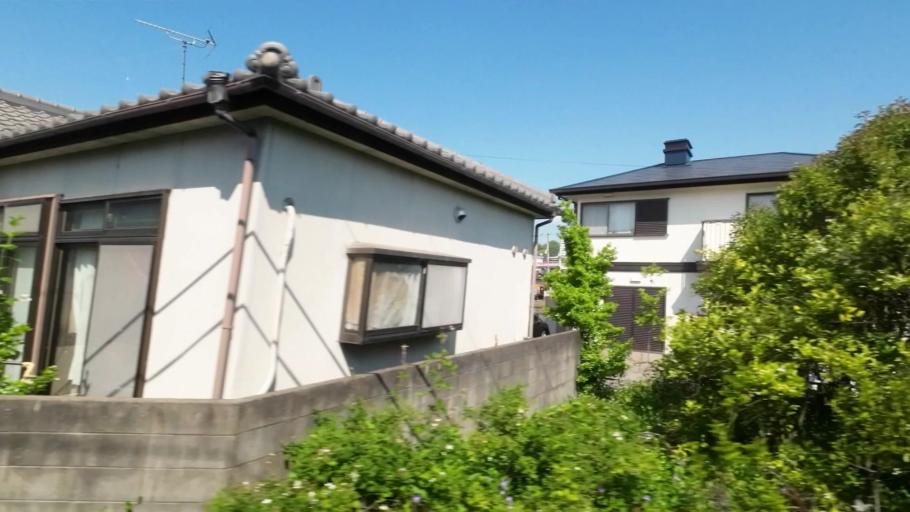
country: JP
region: Kagawa
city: Tadotsu
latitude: 34.2645
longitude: 133.7534
